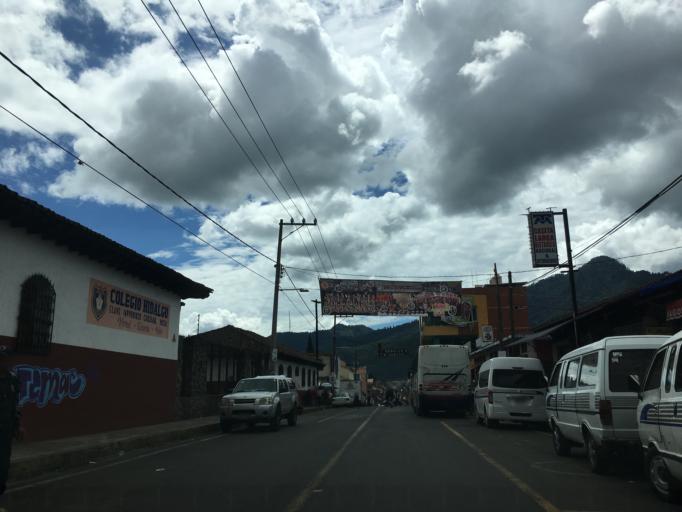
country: MX
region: Michoacan
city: Cheran
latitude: 19.6885
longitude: -101.9560
